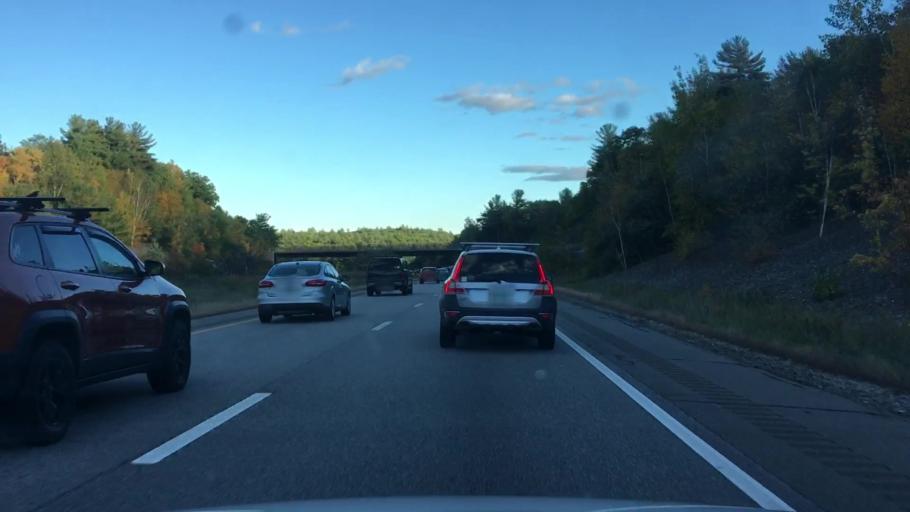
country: US
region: New Hampshire
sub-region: Rockingham County
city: Raymond
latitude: 43.0237
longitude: -71.2337
